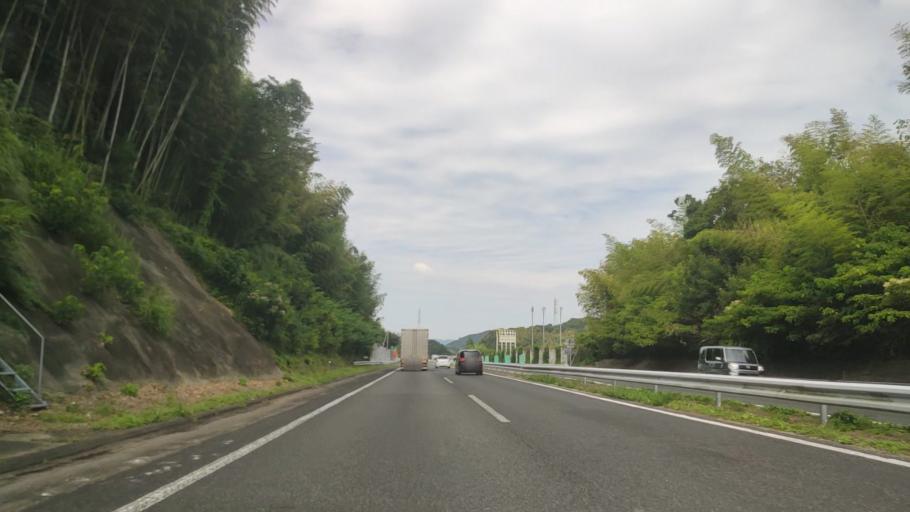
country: JP
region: Wakayama
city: Kainan
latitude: 34.1988
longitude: 135.2336
